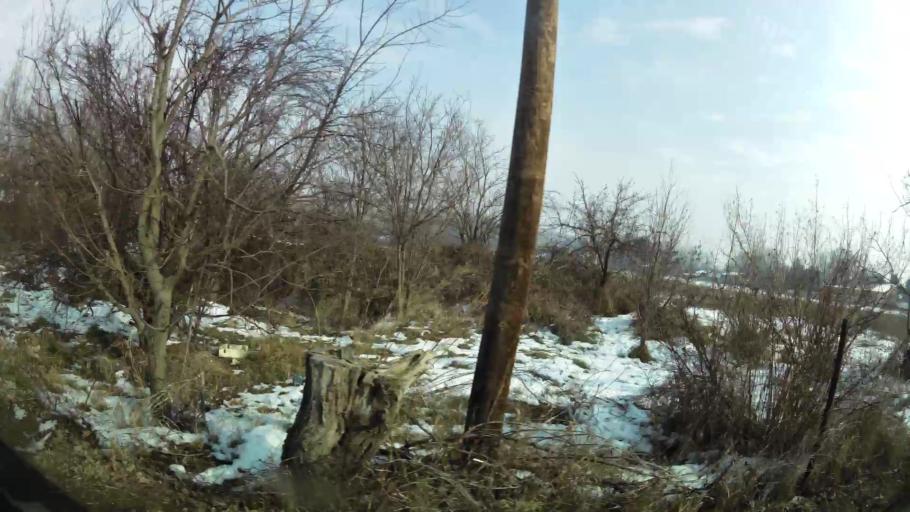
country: MK
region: Suto Orizari
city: Suto Orizare
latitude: 42.0153
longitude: 21.3877
